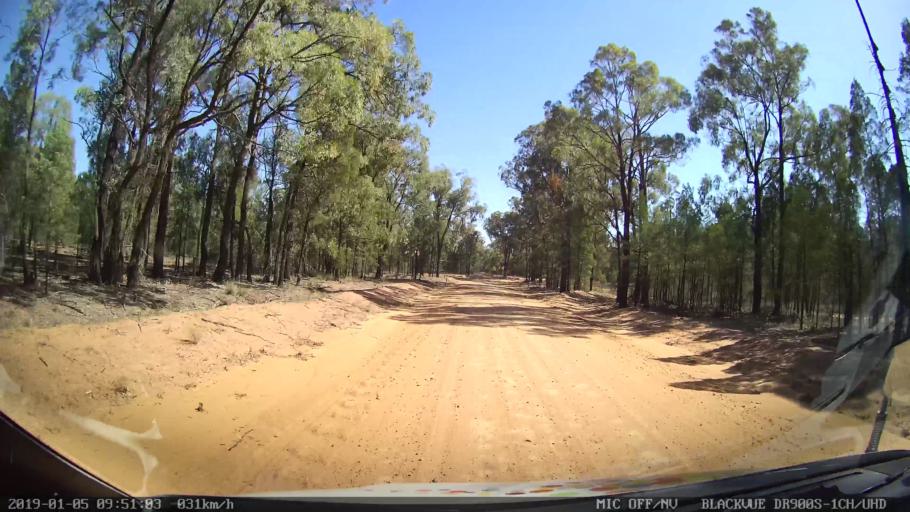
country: AU
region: New South Wales
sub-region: Gilgandra
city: Gilgandra
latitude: -31.6620
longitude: 148.7593
